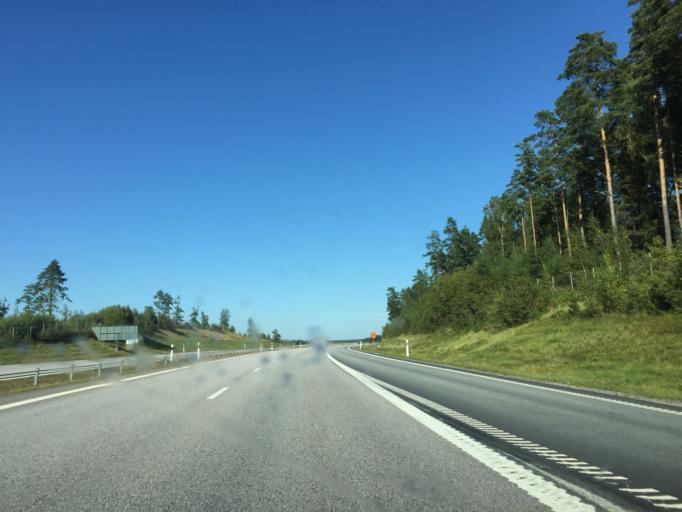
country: SE
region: Vaestmanland
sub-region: Arboga Kommun
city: Arboga
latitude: 59.4162
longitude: 15.7724
